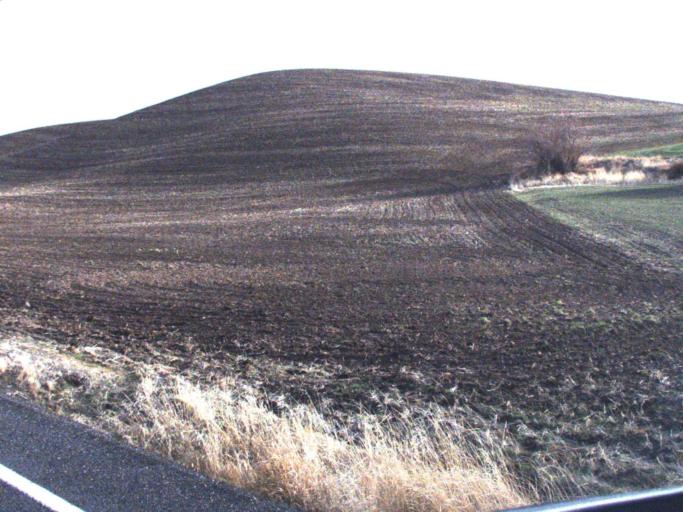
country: US
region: Washington
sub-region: Whitman County
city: Colfax
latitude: 46.7473
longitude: -117.4613
